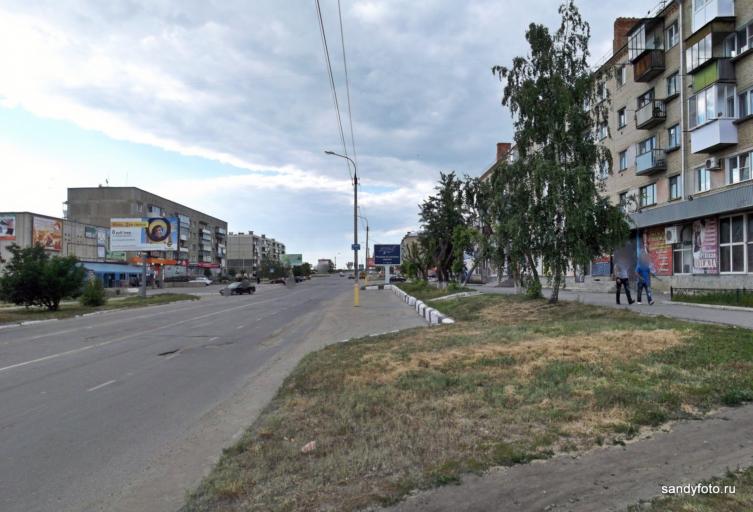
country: RU
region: Chelyabinsk
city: Troitsk
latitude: 54.0775
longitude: 61.5309
